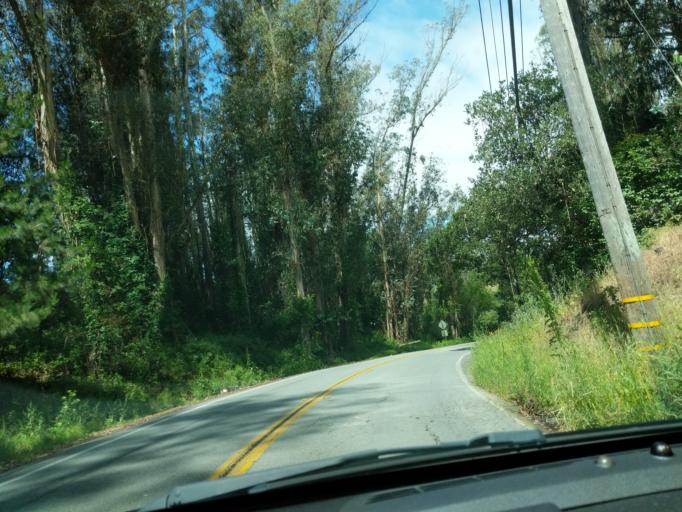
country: US
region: California
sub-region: Santa Cruz County
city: Freedom
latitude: 36.9388
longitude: -121.8041
